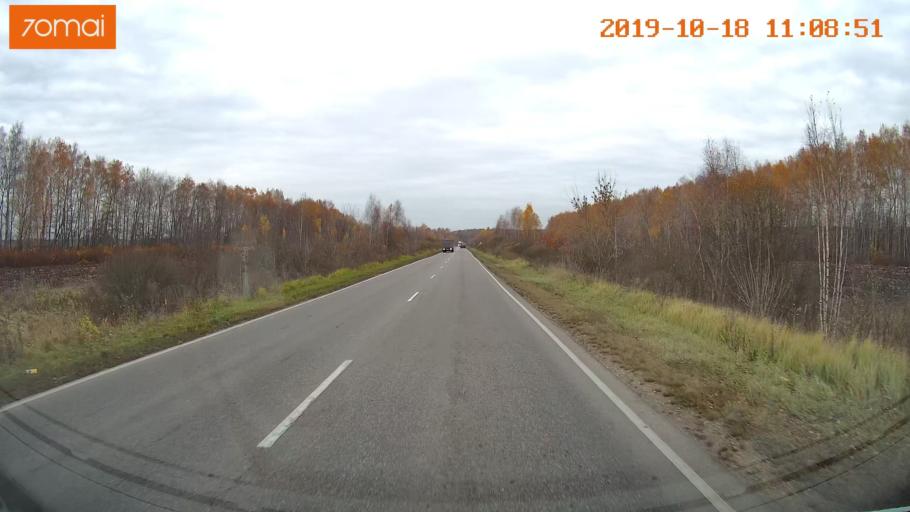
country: RU
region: Tula
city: Kimovsk
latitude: 53.9445
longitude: 38.5345
